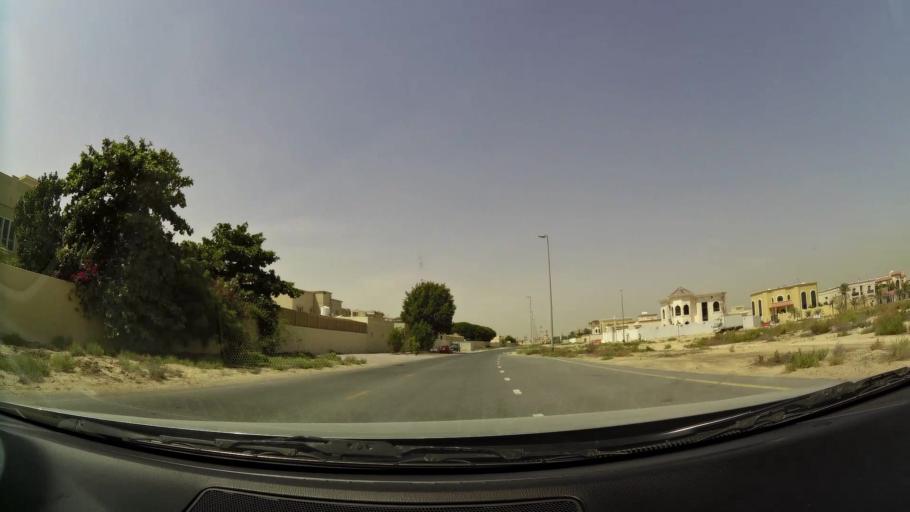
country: AE
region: Ash Shariqah
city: Sharjah
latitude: 25.1838
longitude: 55.4390
